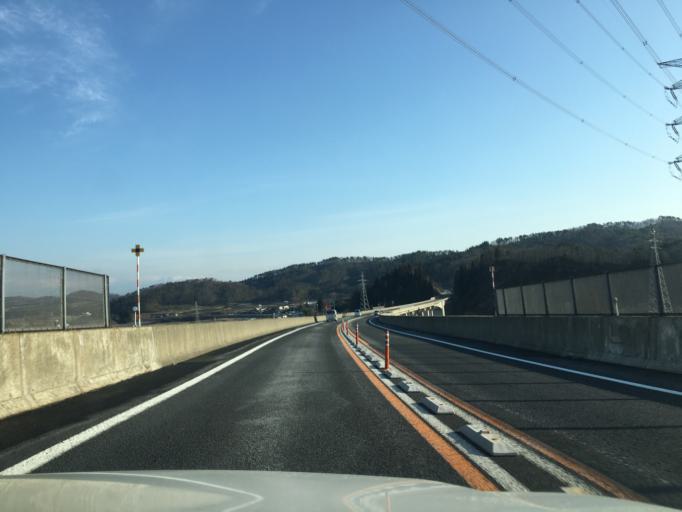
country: JP
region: Yamagata
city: Sagae
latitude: 38.4154
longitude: 140.1891
